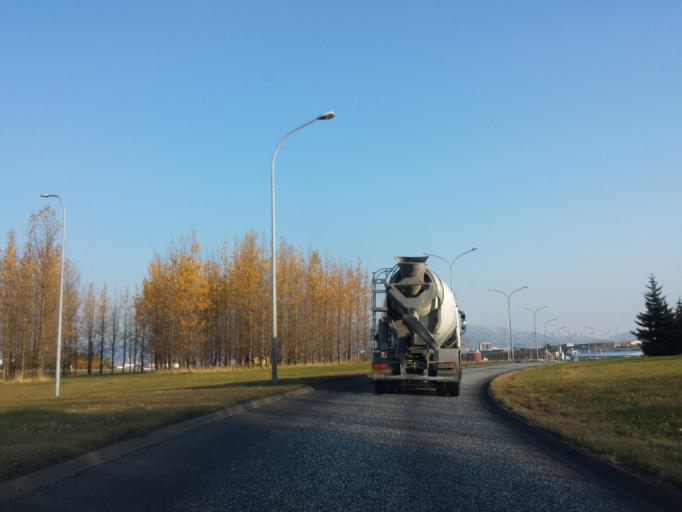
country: IS
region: Capital Region
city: Reykjavik
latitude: 64.1229
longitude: -21.8471
